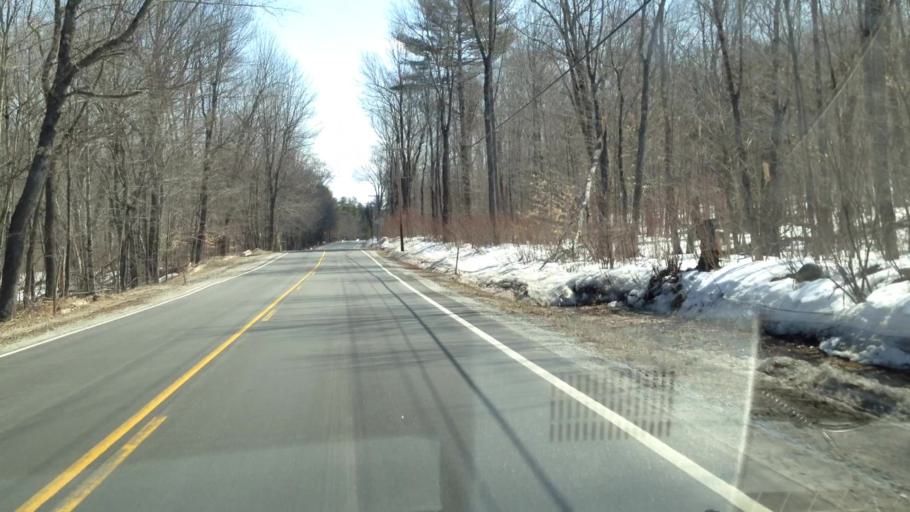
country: US
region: New Hampshire
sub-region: Merrimack County
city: Wilmot
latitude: 43.4601
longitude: -71.9393
